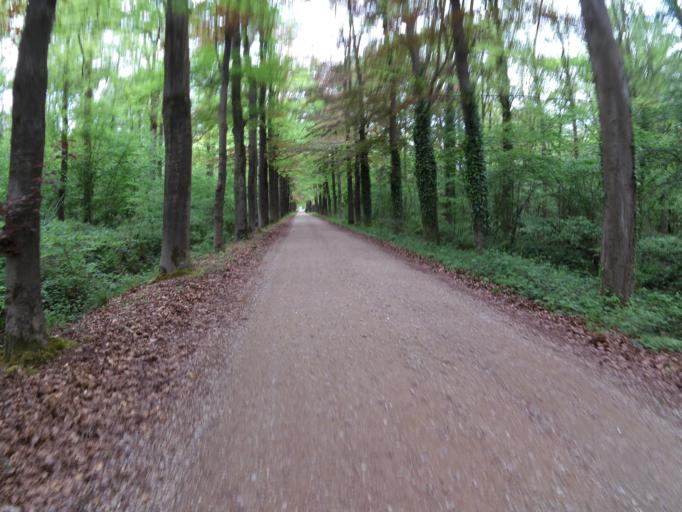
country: NL
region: North Brabant
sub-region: Gemeente Oirschot
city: Oirschot
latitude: 51.5442
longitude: 5.3410
